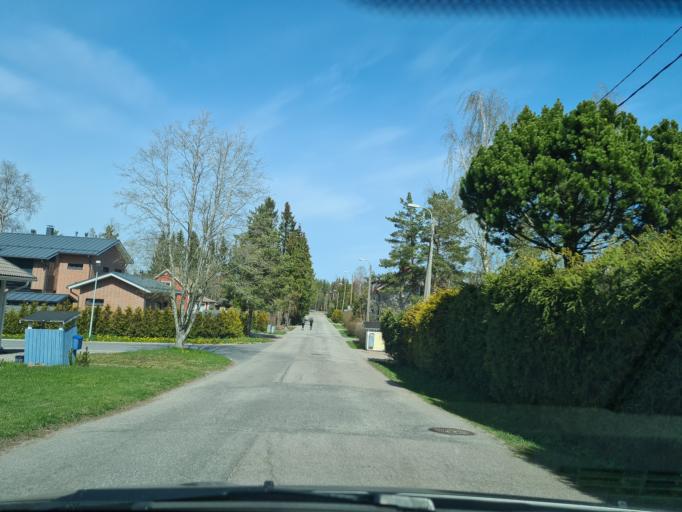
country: FI
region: Uusimaa
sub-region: Helsinki
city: Vantaa
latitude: 60.3300
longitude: 25.0889
